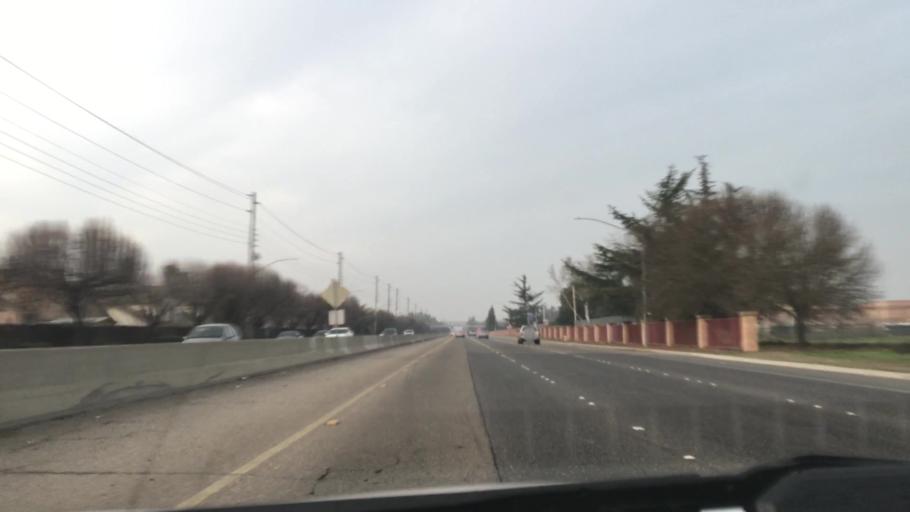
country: US
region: California
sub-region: Stanislaus County
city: Empire
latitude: 37.6442
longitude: -120.9210
